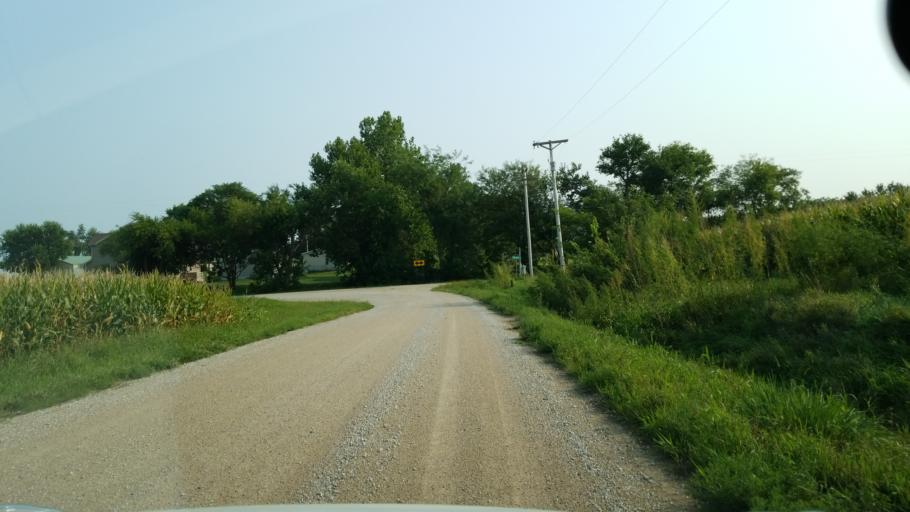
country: US
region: Nebraska
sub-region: Sarpy County
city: Offutt Air Force Base
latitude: 41.0754
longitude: -95.9329
